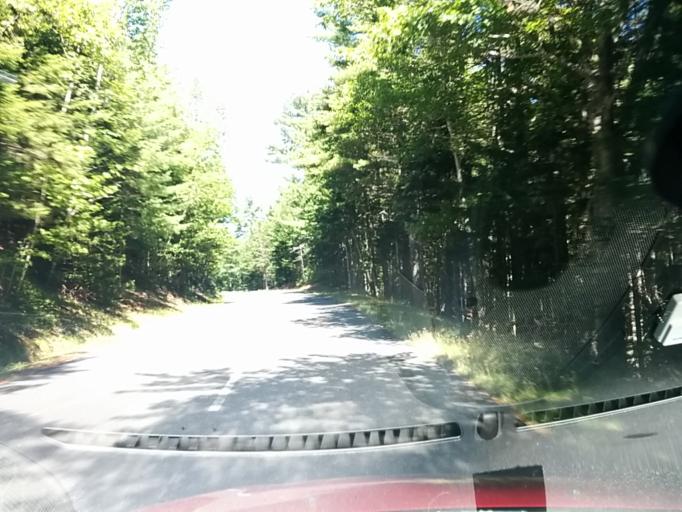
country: US
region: Maine
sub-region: Hancock County
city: Bar Harbor
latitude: 44.3149
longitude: -68.2258
